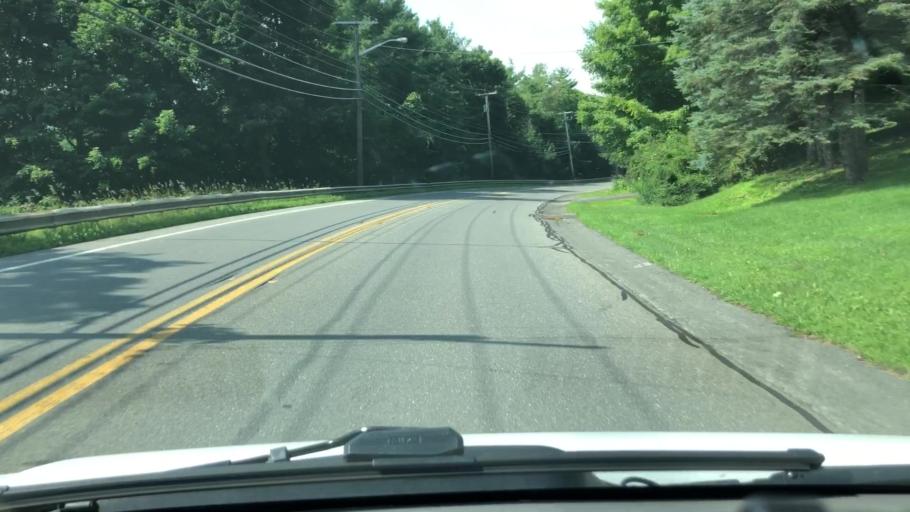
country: US
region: Massachusetts
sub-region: Berkshire County
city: Adams
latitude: 42.5697
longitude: -73.1554
